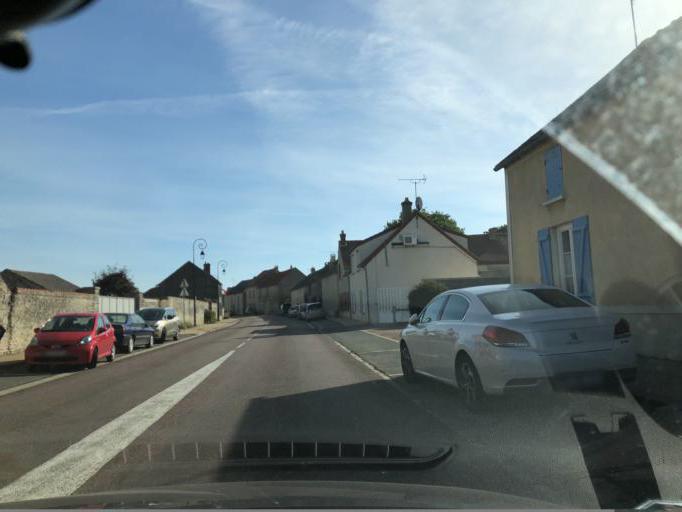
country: FR
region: Ile-de-France
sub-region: Departement de l'Essonne
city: Maisse
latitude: 48.3422
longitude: 2.3208
